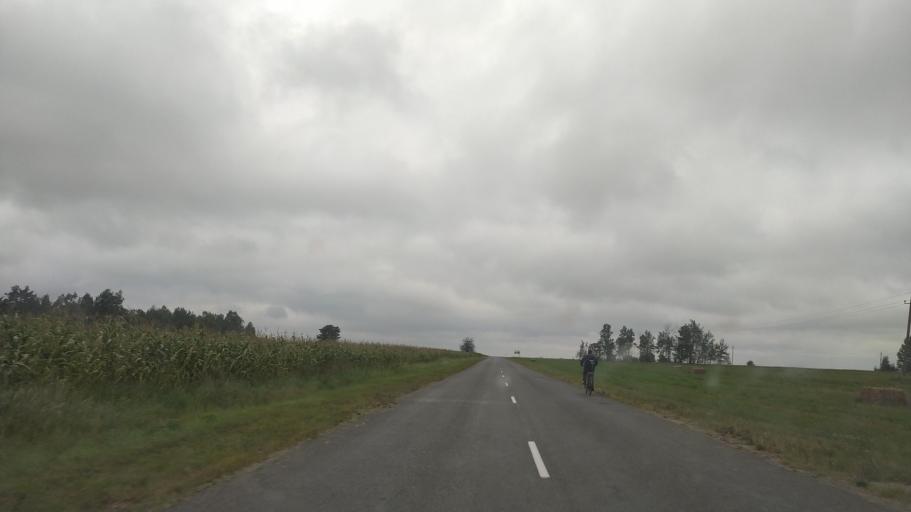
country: BY
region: Brest
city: Byaroza
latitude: 52.5640
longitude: 24.9034
